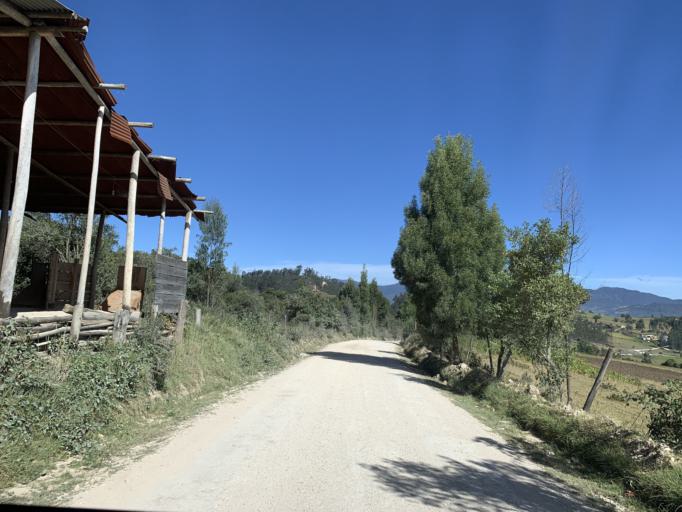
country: CO
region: Boyaca
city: Tuta
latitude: 5.7055
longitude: -73.1510
